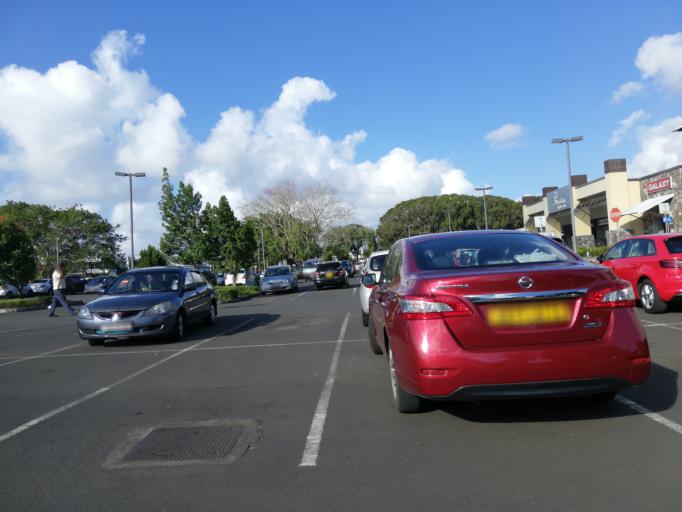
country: MU
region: Moka
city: Verdun
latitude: -20.2259
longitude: 57.5374
